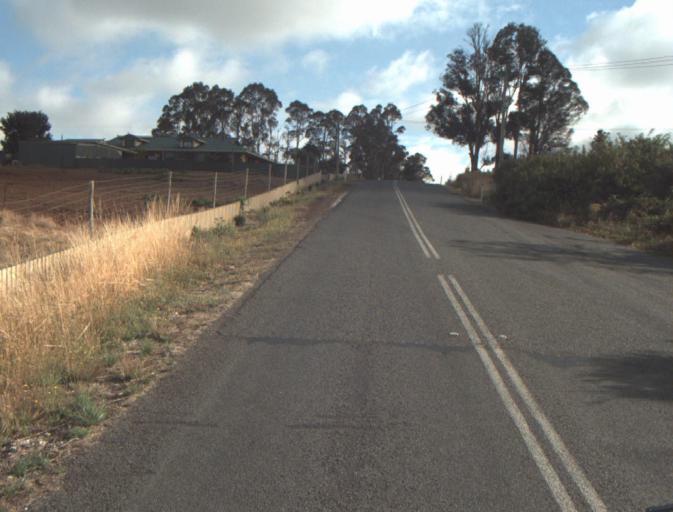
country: AU
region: Tasmania
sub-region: Dorset
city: Bridport
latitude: -41.1707
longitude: 147.2301
